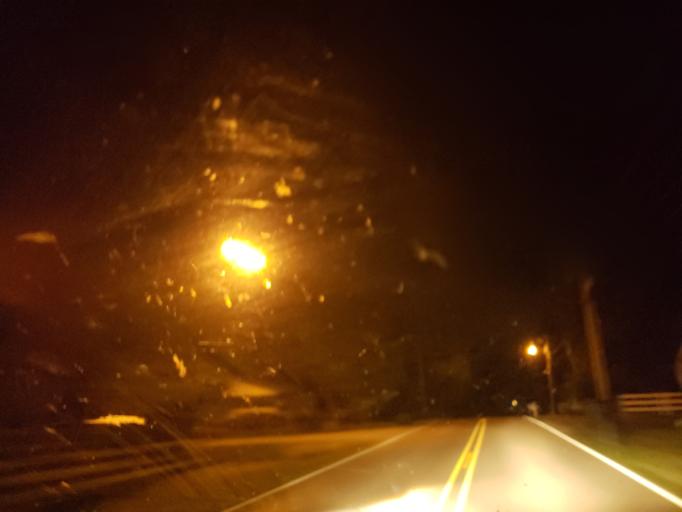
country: US
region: Alabama
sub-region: Madison County
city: Hazel Green
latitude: 34.9667
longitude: -86.5402
